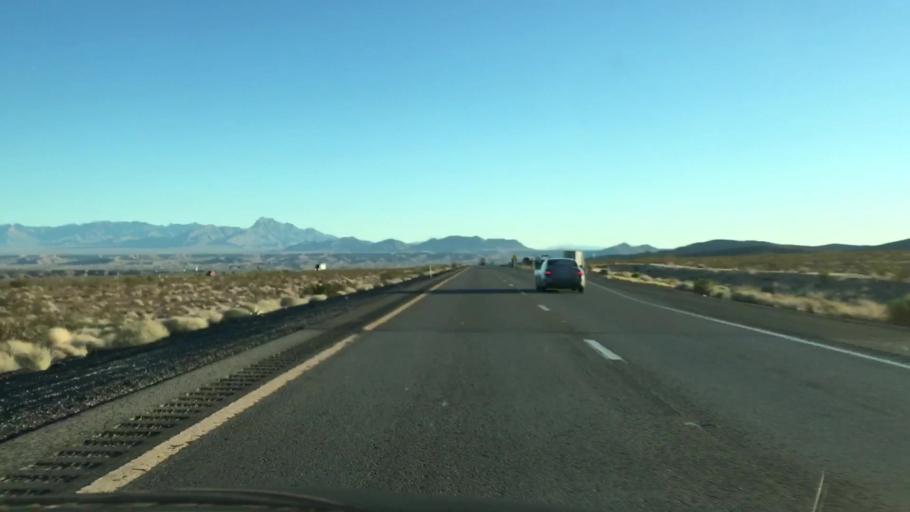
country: US
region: Nevada
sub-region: Clark County
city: Moapa Town
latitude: 36.6258
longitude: -114.6114
